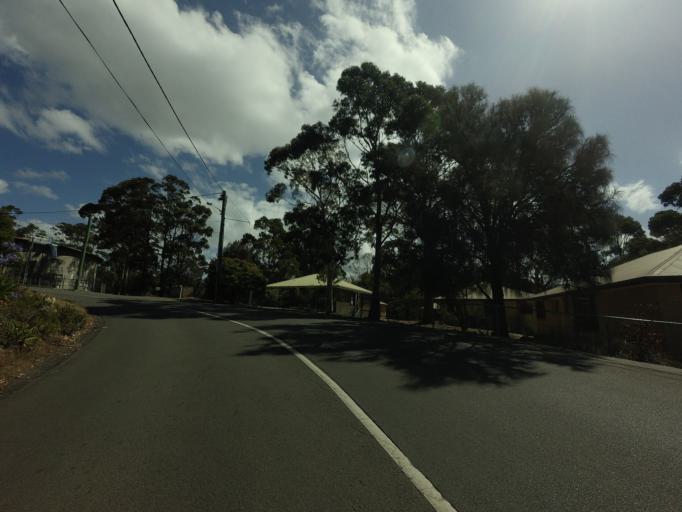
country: AU
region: Tasmania
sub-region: Hobart
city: Dynnyrne
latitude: -42.9111
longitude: 147.3225
